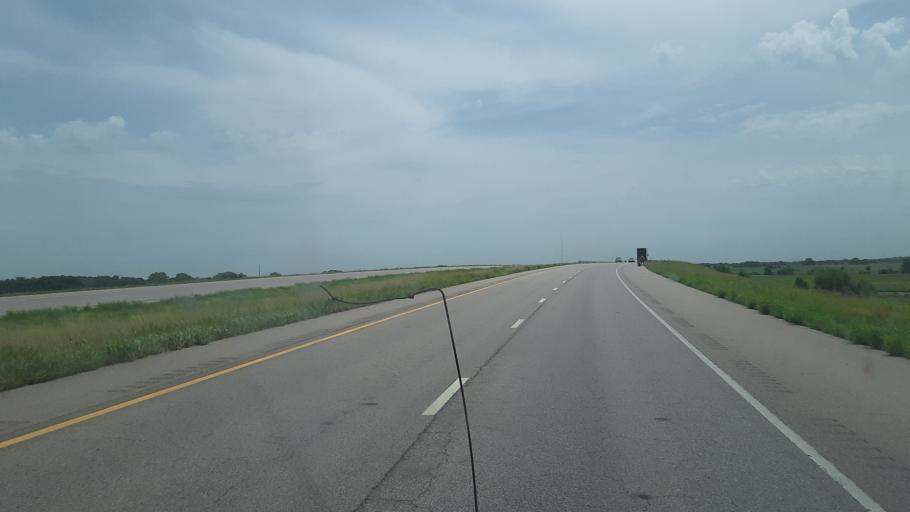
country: US
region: Kansas
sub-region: Butler County
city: Towanda
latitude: 37.8062
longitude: -96.9852
